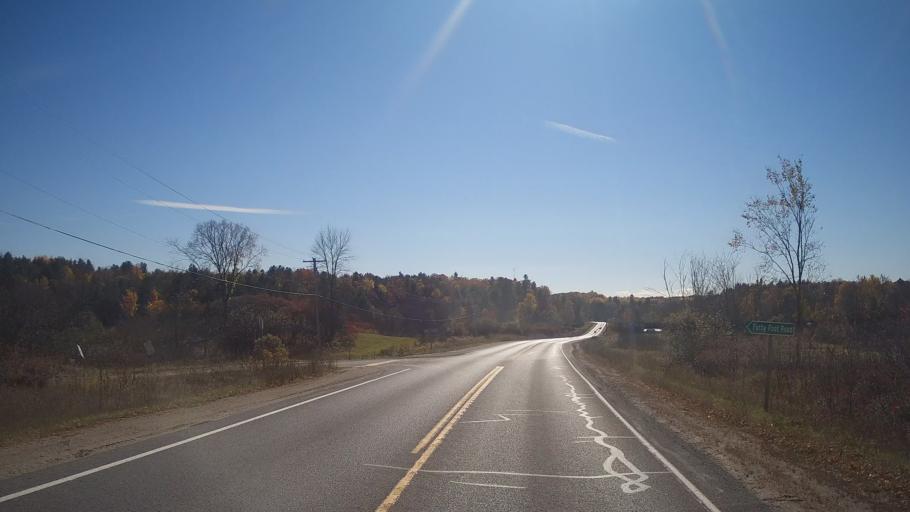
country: CA
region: Ontario
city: Kingston
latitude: 44.5552
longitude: -76.6738
